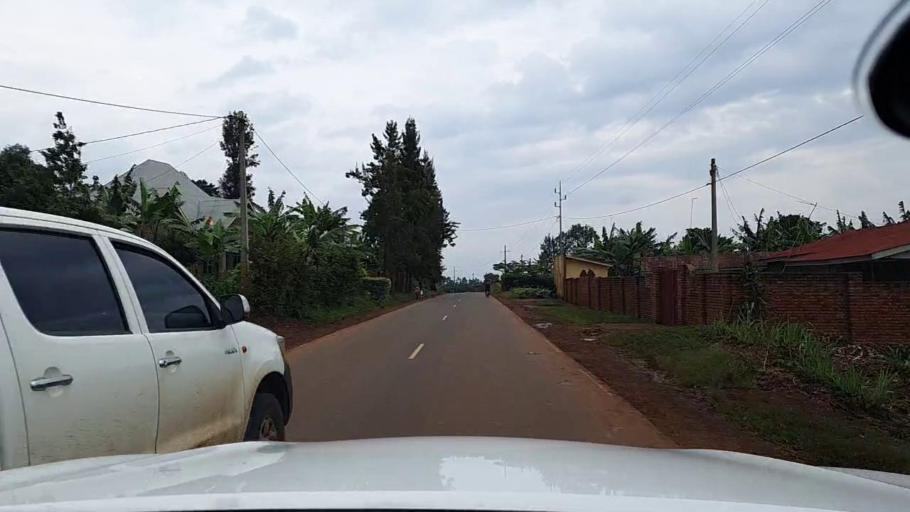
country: RW
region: Western Province
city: Cyangugu
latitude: -2.6197
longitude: 28.9456
